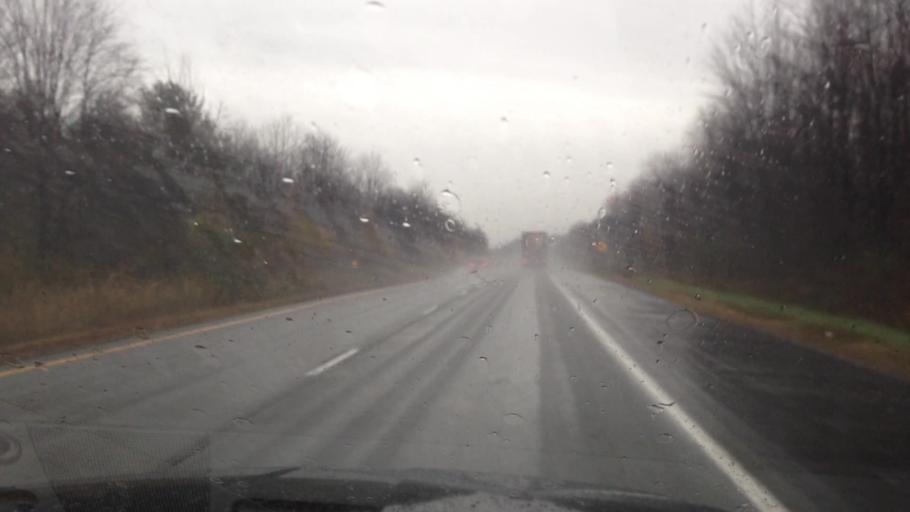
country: CA
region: Ontario
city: Bourget
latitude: 45.3133
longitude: -75.2275
